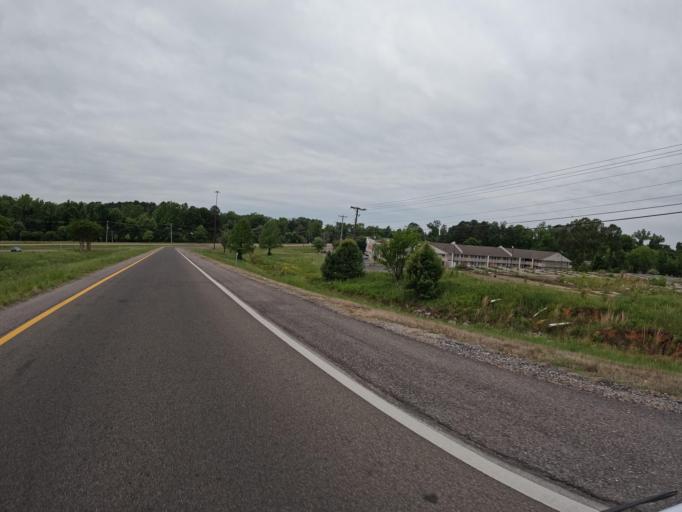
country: US
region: Mississippi
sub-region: Lee County
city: Tupelo
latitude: 34.2754
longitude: -88.7164
